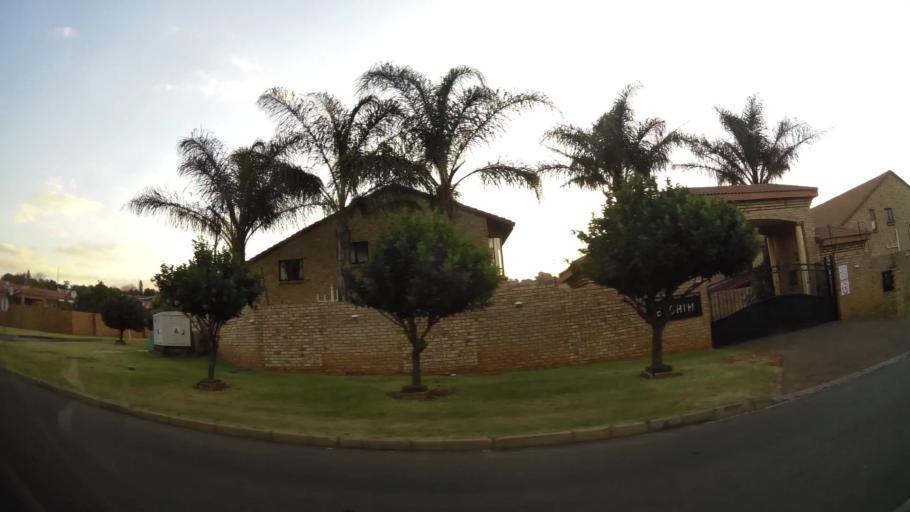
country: ZA
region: Gauteng
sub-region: West Rand District Municipality
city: Krugersdorp
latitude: -26.0735
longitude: 27.7895
